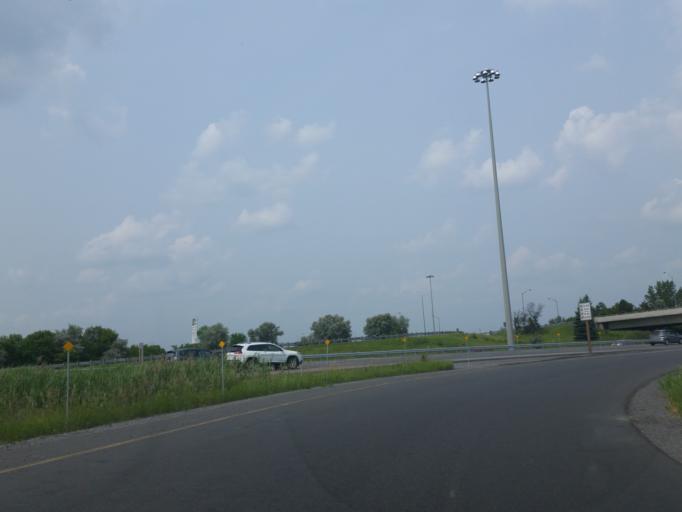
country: CA
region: Ontario
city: Bells Corners
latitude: 45.3192
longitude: -75.8872
